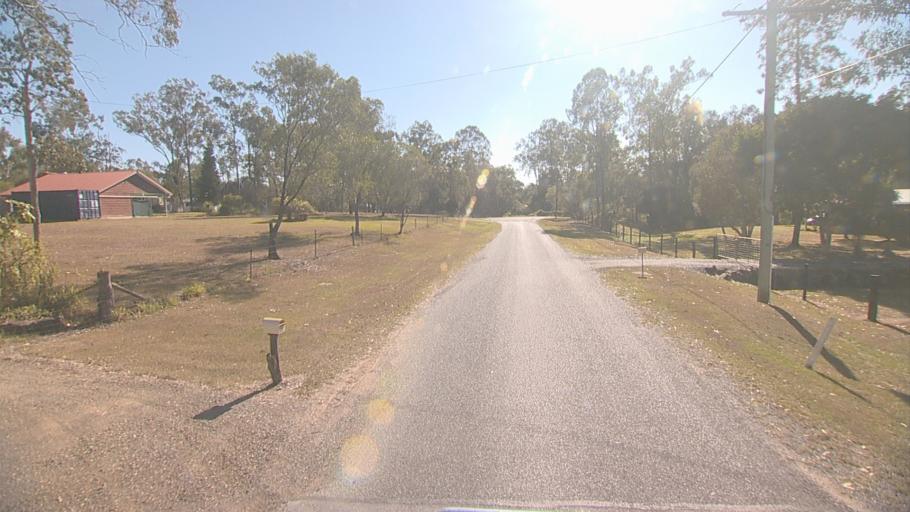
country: AU
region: Queensland
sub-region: Logan
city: North Maclean
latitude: -27.8254
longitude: 153.0482
